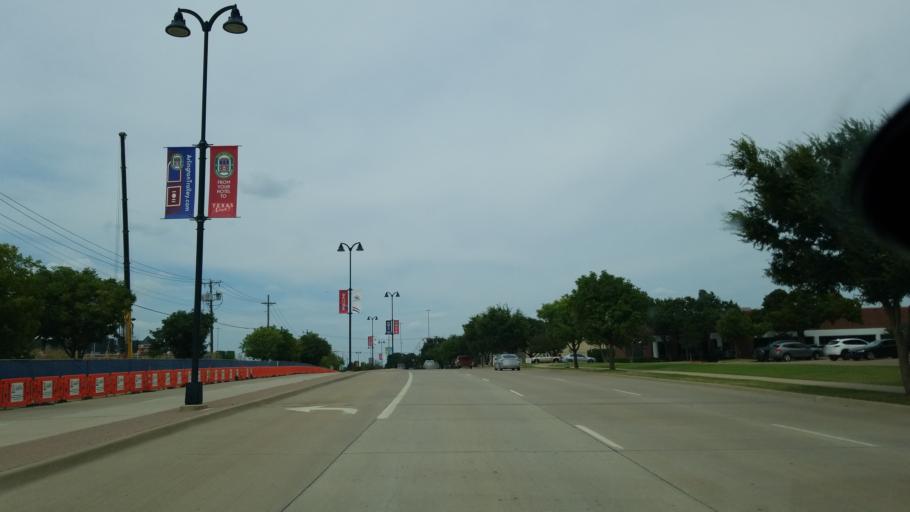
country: US
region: Texas
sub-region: Tarrant County
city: Arlington
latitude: 32.7464
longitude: -97.0821
